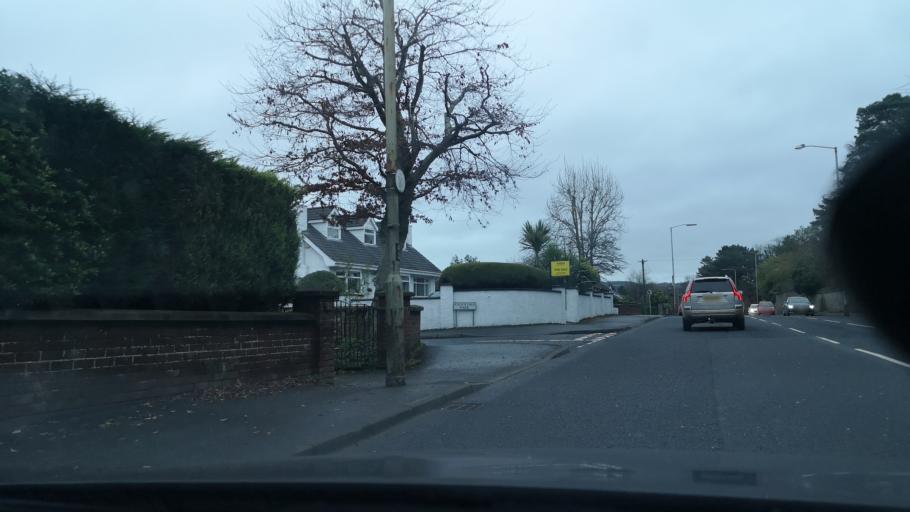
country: GB
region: Northern Ireland
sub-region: Castlereagh District
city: Castlereagh
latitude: 54.5868
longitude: -5.8592
